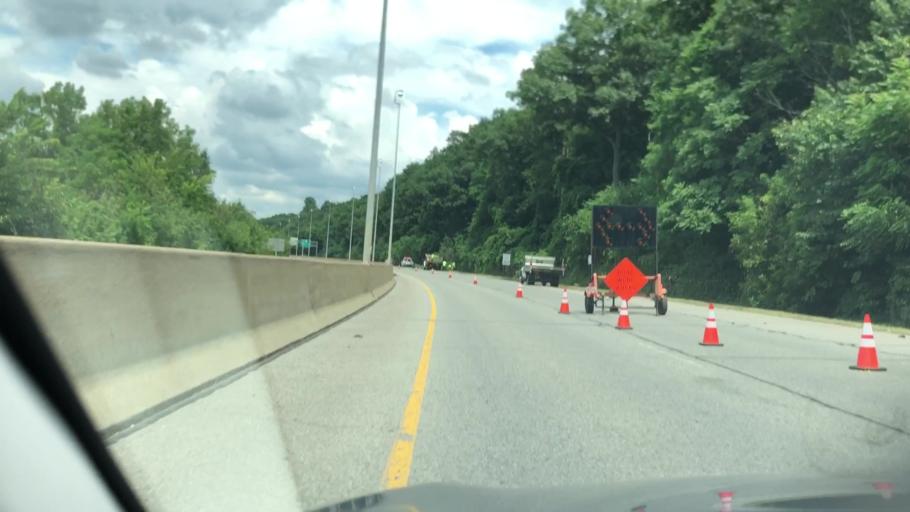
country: US
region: Ohio
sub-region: Stark County
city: Massillon
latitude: 40.7734
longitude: -81.5187
